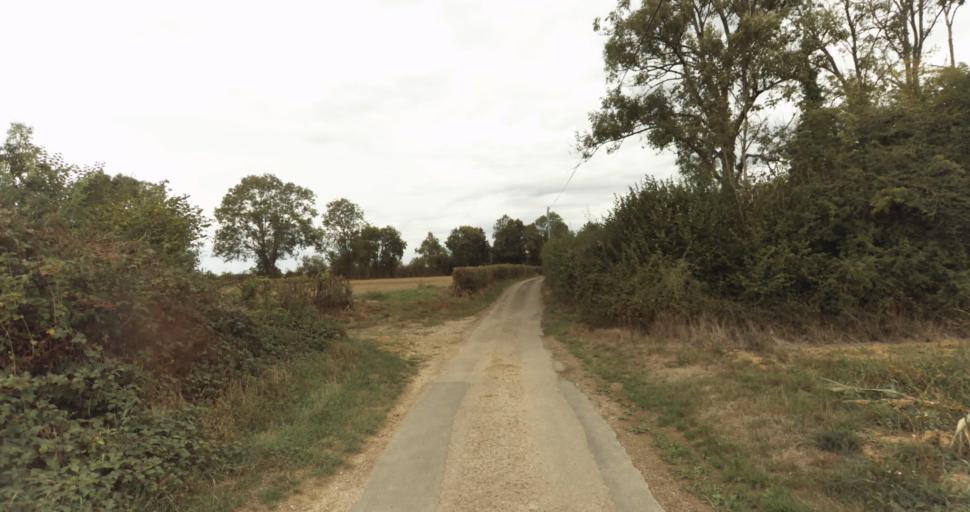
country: FR
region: Lower Normandy
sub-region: Departement de l'Orne
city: Vimoutiers
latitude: 48.9195
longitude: 0.3040
